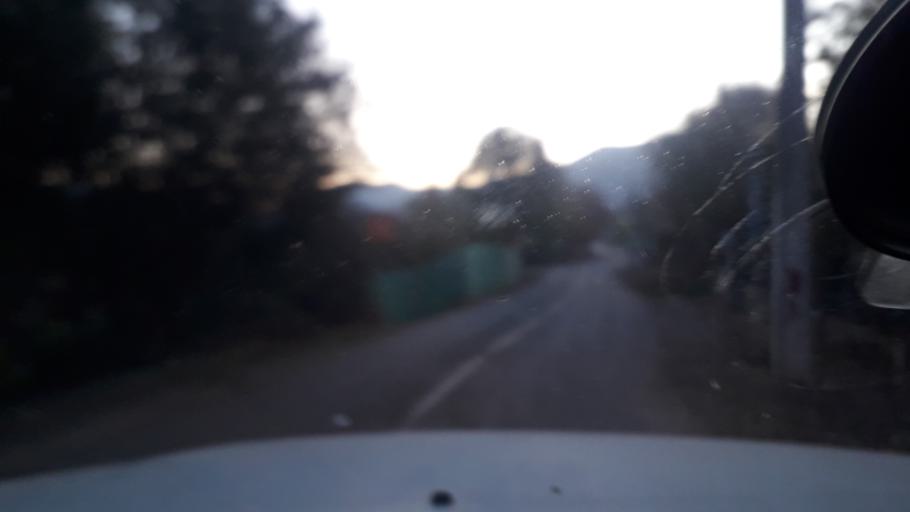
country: CL
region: Valparaiso
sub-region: Provincia de Marga Marga
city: Limache
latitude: -33.1686
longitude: -71.1394
